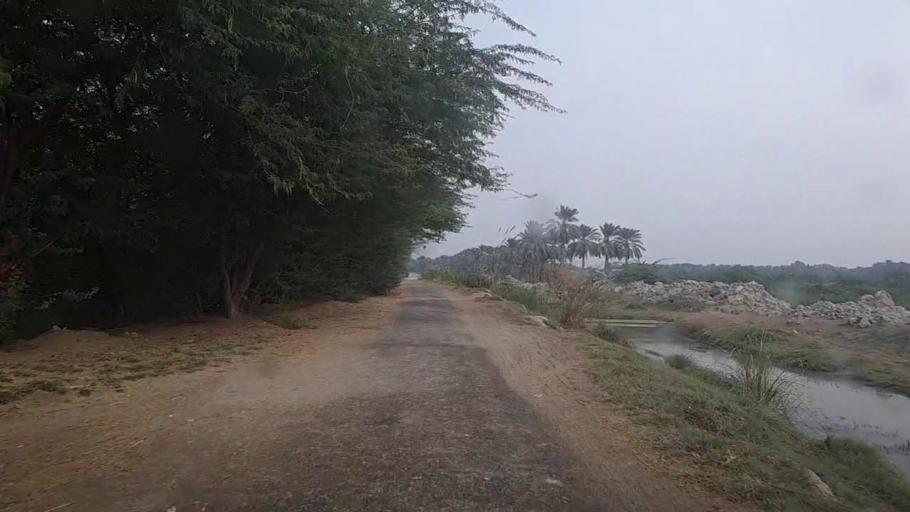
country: PK
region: Sindh
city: Gambat
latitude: 27.3867
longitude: 68.5902
